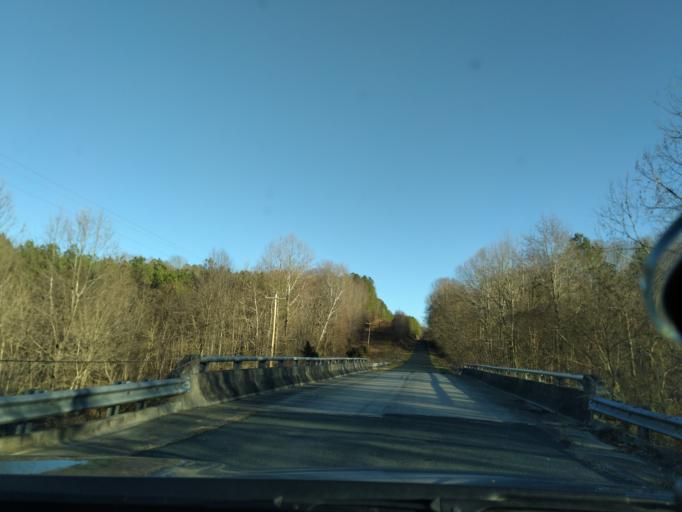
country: US
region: Virginia
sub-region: Appomattox County
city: Appomattox
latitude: 37.3740
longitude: -78.6350
